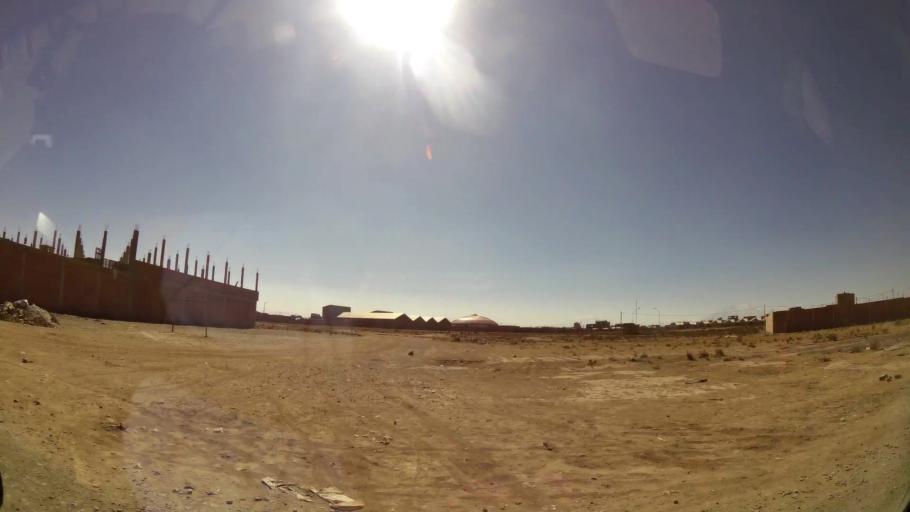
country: BO
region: La Paz
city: La Paz
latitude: -16.6144
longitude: -68.1942
